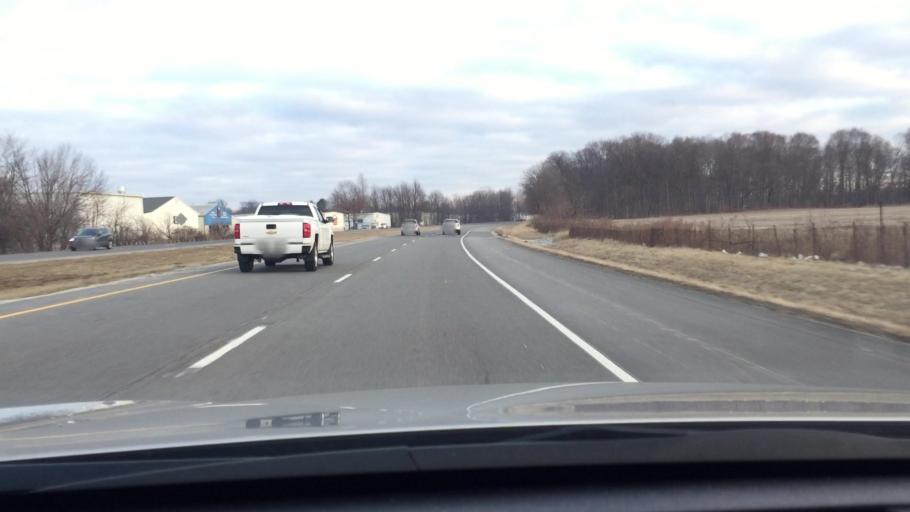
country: US
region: Indiana
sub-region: Hamilton County
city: Noblesville
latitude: 40.0092
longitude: -86.0040
